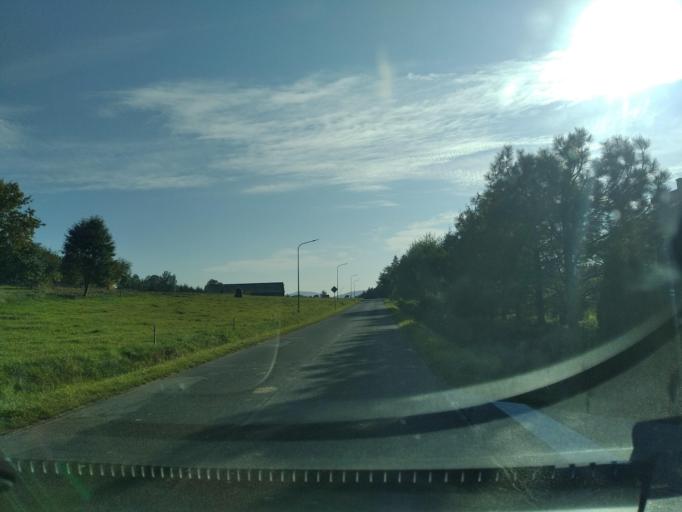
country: PL
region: Subcarpathian Voivodeship
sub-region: Powiat krosnienski
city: Sieniawa
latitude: 49.5685
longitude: 21.9388
